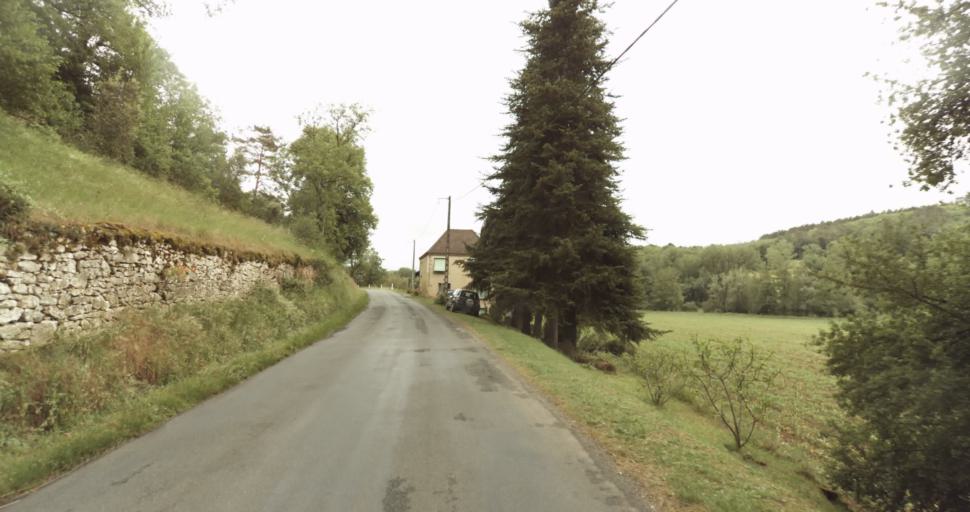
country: FR
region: Aquitaine
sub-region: Departement de la Dordogne
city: Beaumont-du-Perigord
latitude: 44.7692
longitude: 0.8011
